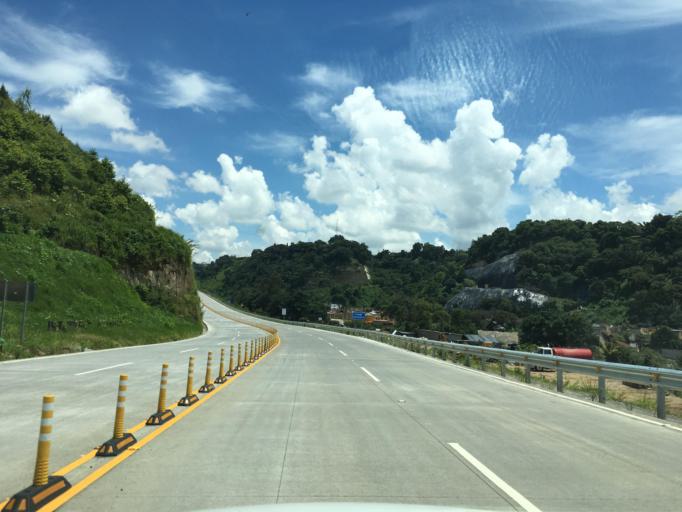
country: GT
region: Guatemala
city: Petapa
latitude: 14.5432
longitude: -90.5336
